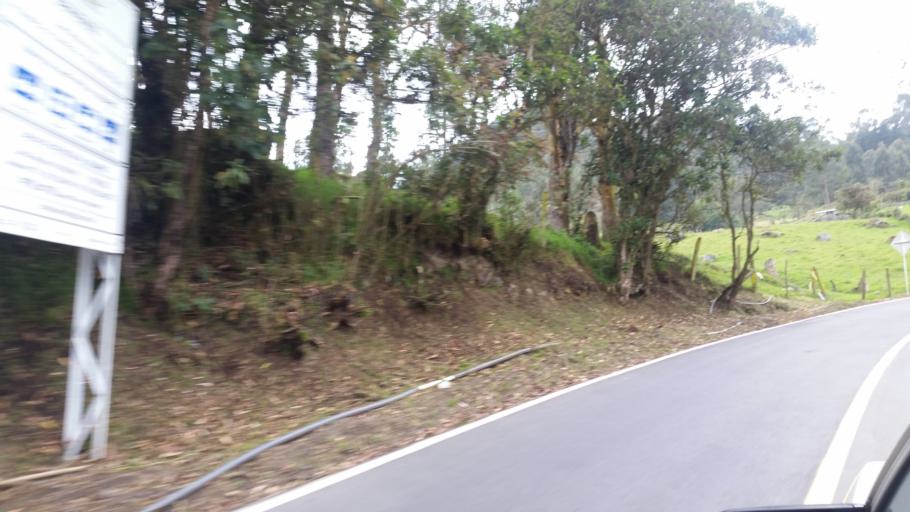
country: CO
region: Cundinamarca
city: Choachi
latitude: 4.5552
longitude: -73.9430
